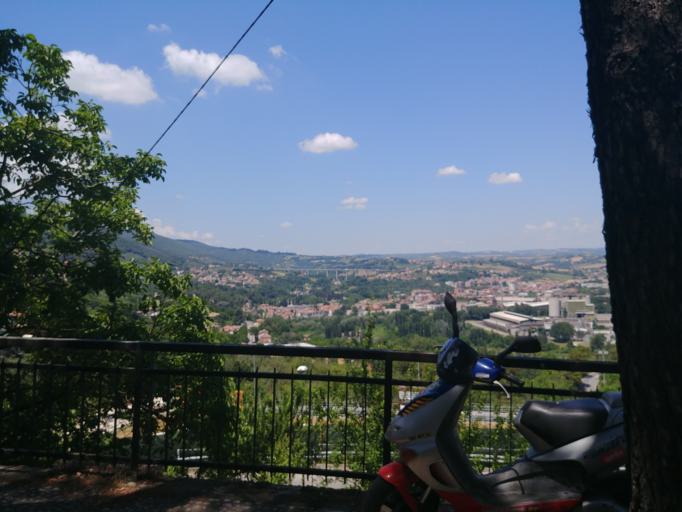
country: IT
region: Umbria
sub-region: Provincia di Terni
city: Narni
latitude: 42.5174
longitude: 12.5217
